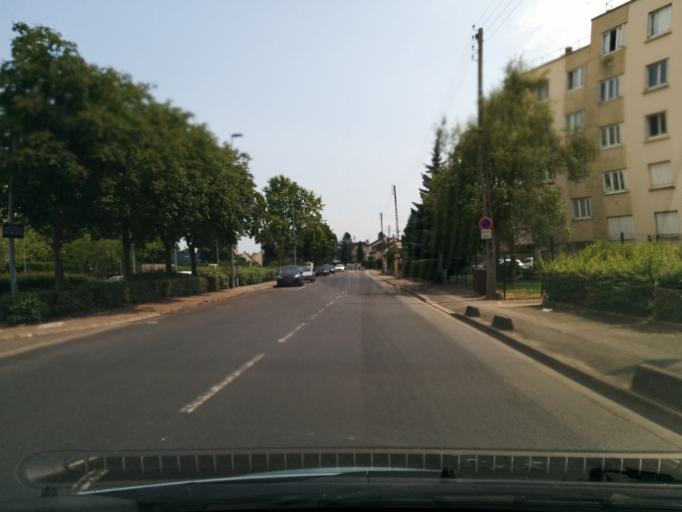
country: FR
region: Ile-de-France
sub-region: Departement des Yvelines
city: Mantes-la-Jolie
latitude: 48.9991
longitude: 1.7036
